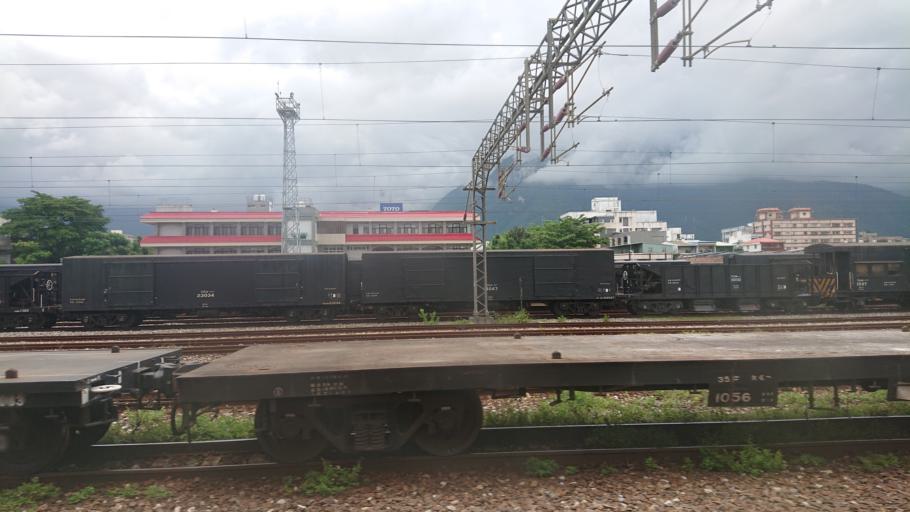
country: TW
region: Taiwan
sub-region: Hualien
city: Hualian
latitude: 23.9942
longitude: 121.6014
